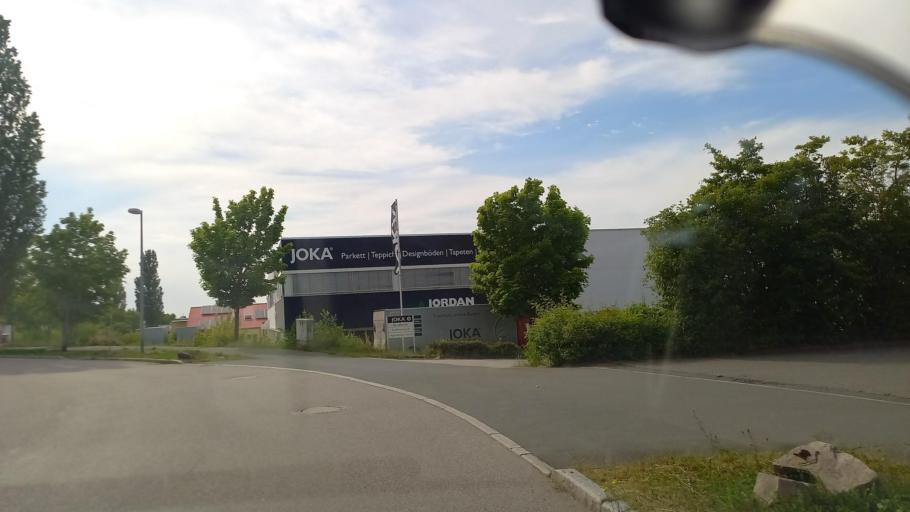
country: DE
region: Saxony
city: Reinsdorf
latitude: 50.6915
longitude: 12.5604
